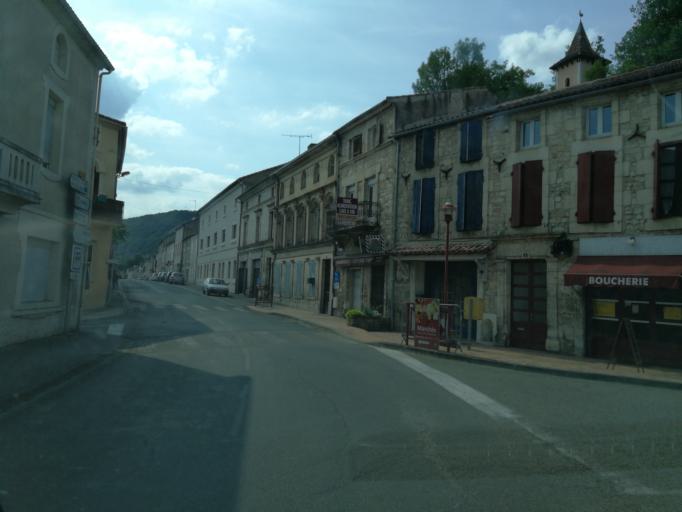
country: FR
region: Aquitaine
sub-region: Departement du Lot-et-Garonne
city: Montayral
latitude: 44.4976
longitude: 0.9884
